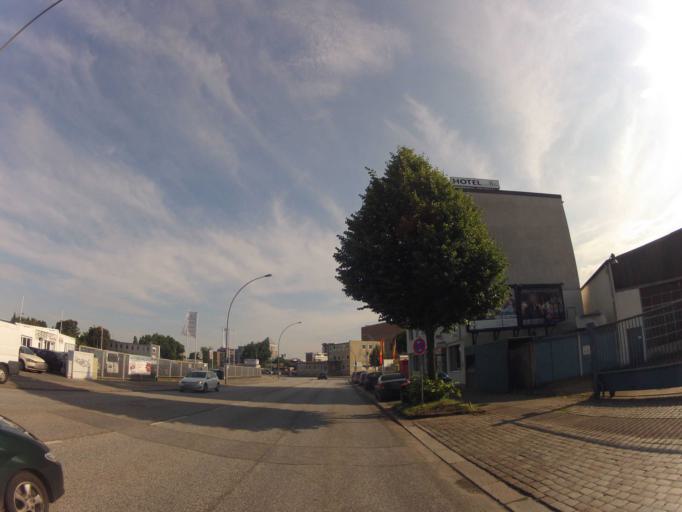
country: DE
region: Hamburg
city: Hammerbrook
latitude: 53.5450
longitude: 10.0402
